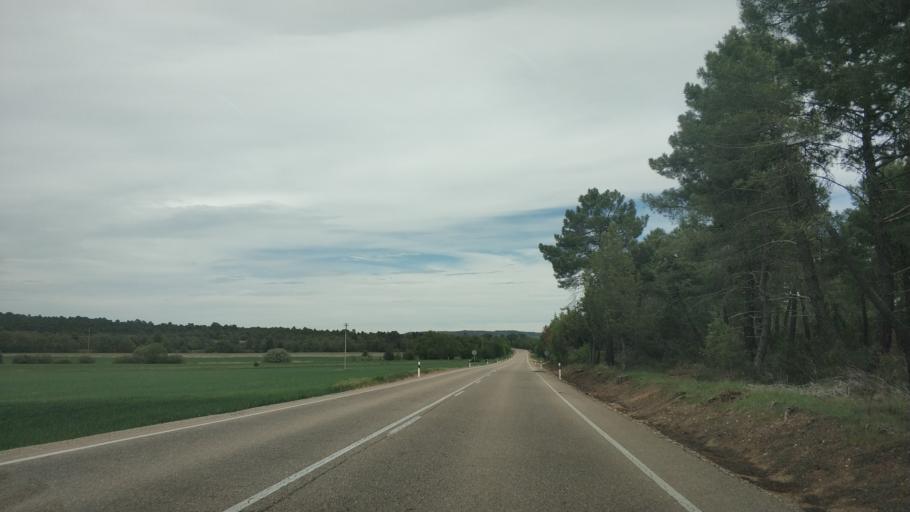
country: ES
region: Castille and Leon
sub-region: Provincia de Soria
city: Bayubas de Abajo
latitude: 41.5077
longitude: -2.9067
